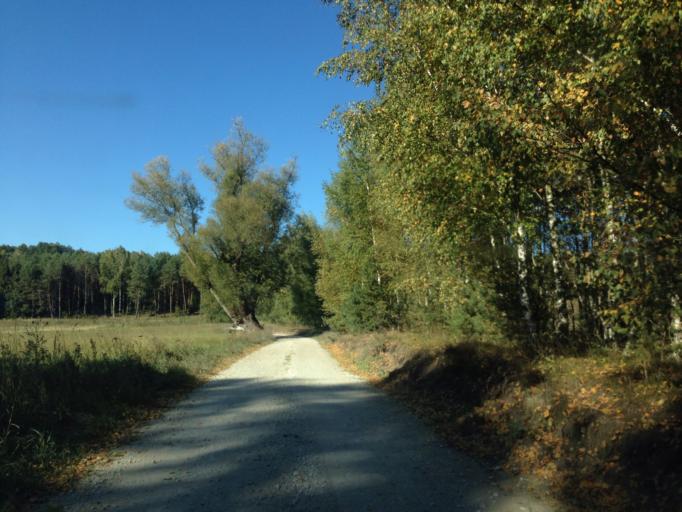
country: PL
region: Kujawsko-Pomorskie
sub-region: Powiat brodnicki
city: Gorzno
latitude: 53.2315
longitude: 19.7005
